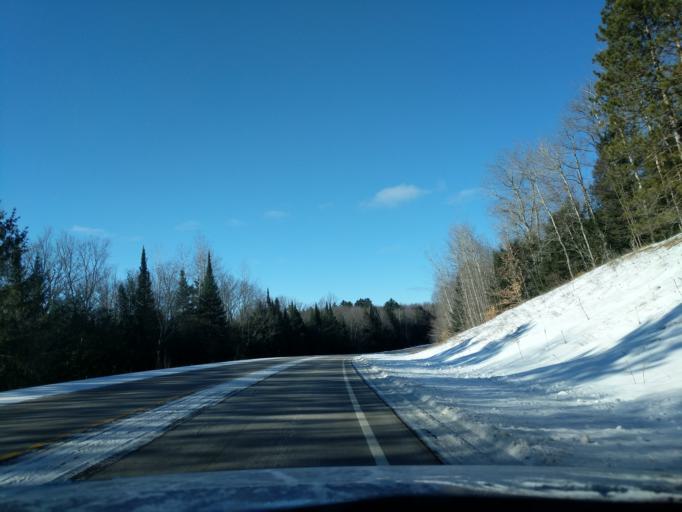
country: US
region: Wisconsin
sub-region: Menominee County
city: Keshena
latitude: 45.1294
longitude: -88.6672
